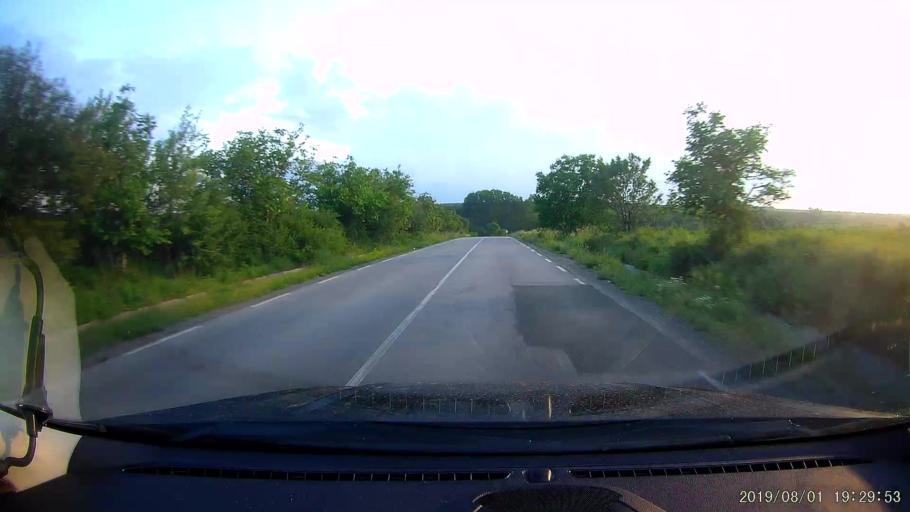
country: BG
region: Burgas
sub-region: Obshtina Sungurlare
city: Sungurlare
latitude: 42.8208
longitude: 26.8995
